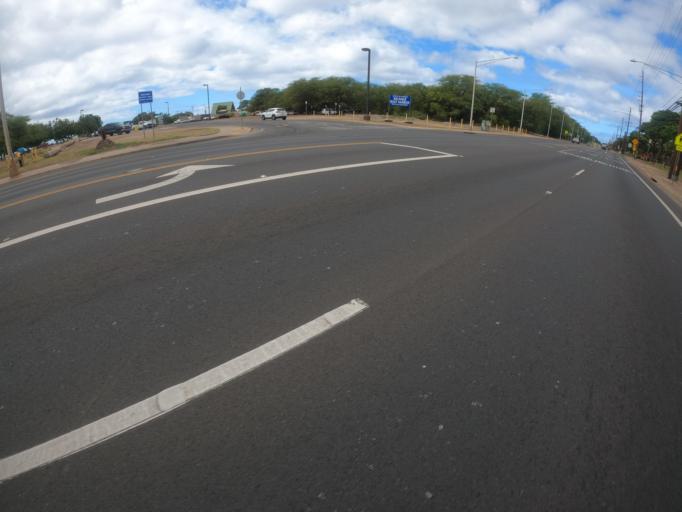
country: US
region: Hawaii
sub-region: Honolulu County
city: Waianae
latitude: 21.4525
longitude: -158.1946
